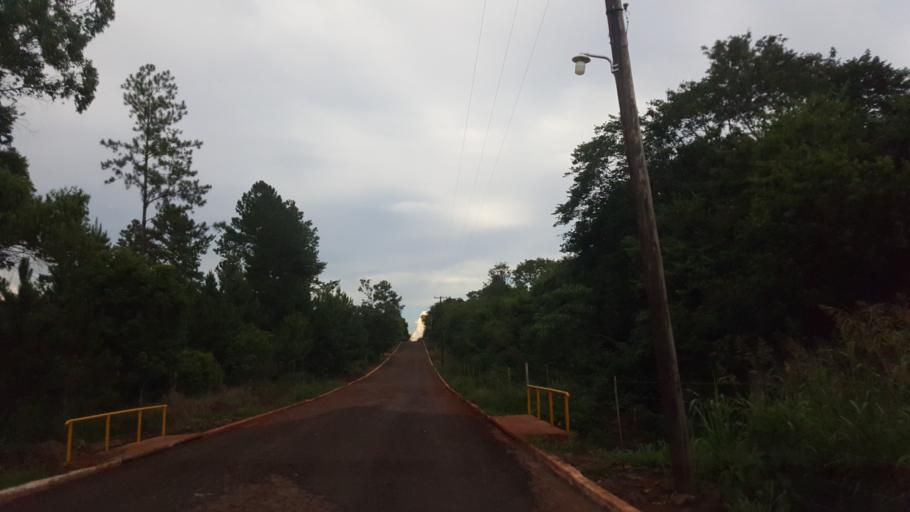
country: AR
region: Misiones
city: Jardin America
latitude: -27.0812
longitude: -55.2864
